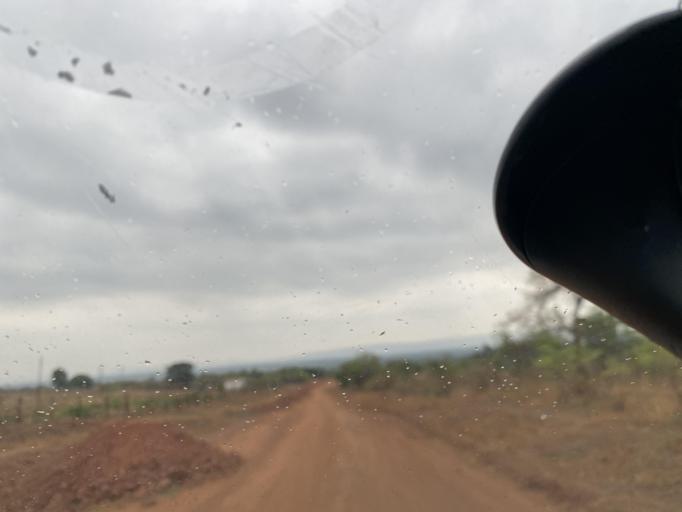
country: ZM
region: Lusaka
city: Chongwe
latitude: -15.1701
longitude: 28.7642
